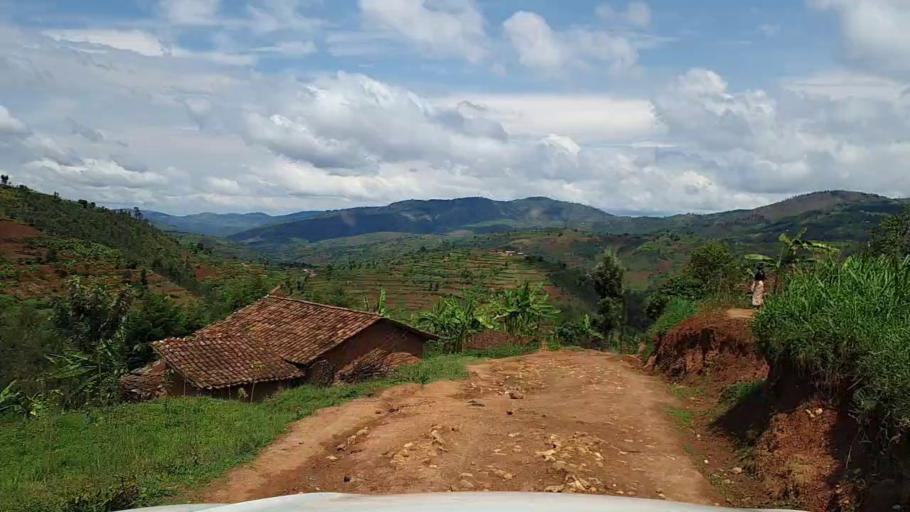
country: RW
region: Southern Province
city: Gikongoro
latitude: -2.3586
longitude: 29.5490
